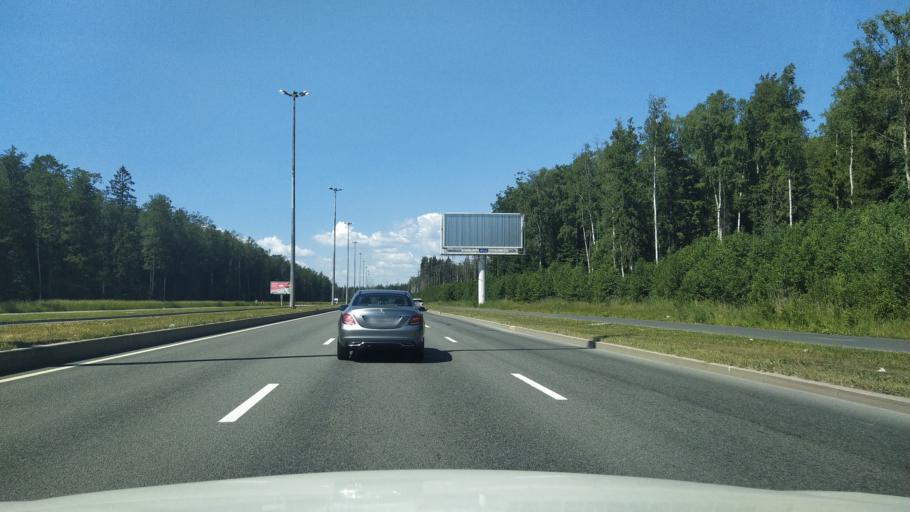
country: RU
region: Leningrad
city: Untolovo
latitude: 60.0565
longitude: 30.2229
